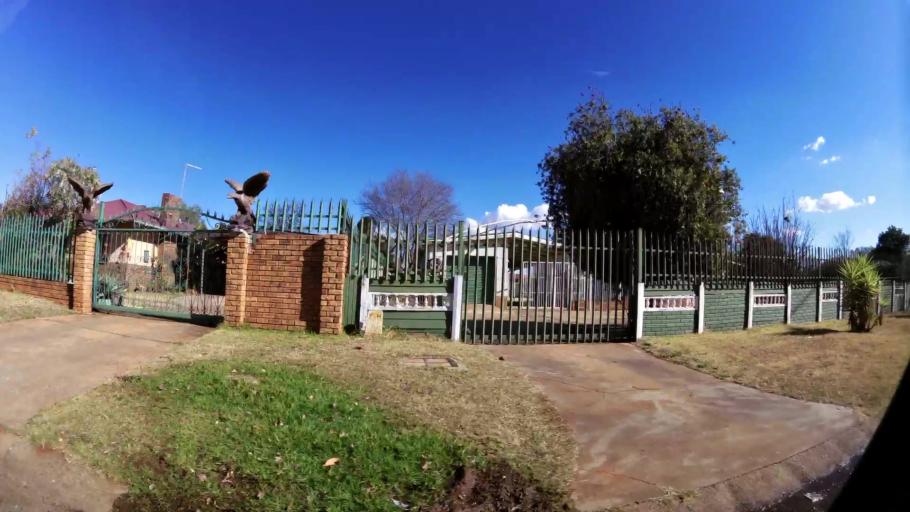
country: ZA
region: Gauteng
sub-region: West Rand District Municipality
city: Carletonville
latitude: -26.3599
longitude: 27.3767
